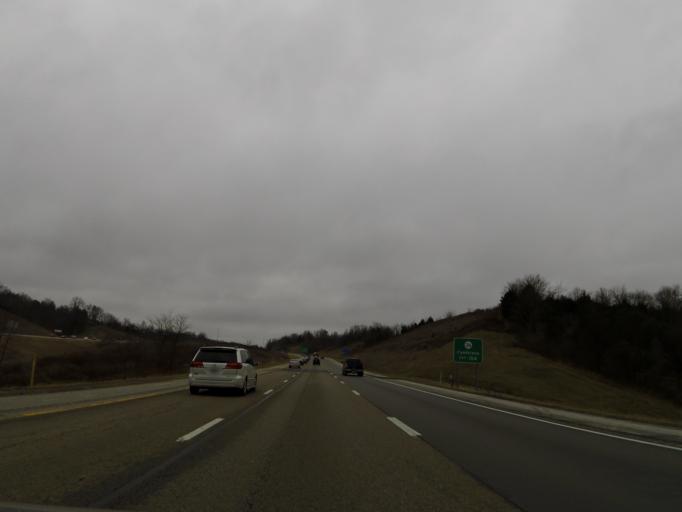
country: US
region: Kentucky
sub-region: Grant County
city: Williamstown
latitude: 38.6379
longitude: -84.5835
